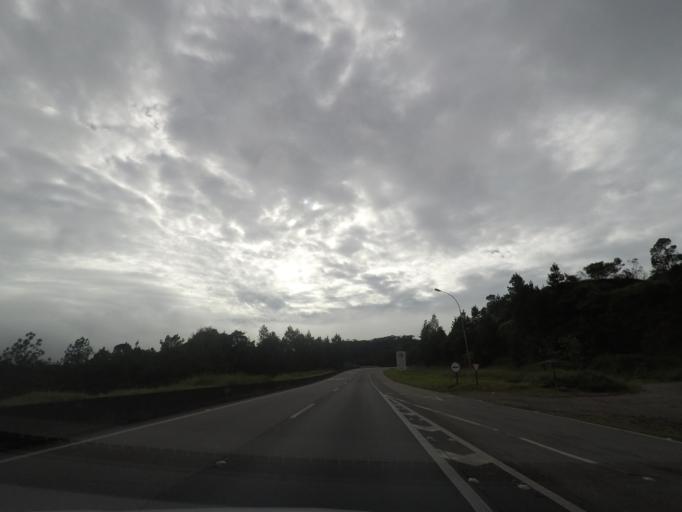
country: BR
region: Parana
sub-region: Campina Grande Do Sul
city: Campina Grande do Sul
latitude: -25.1082
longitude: -48.8357
